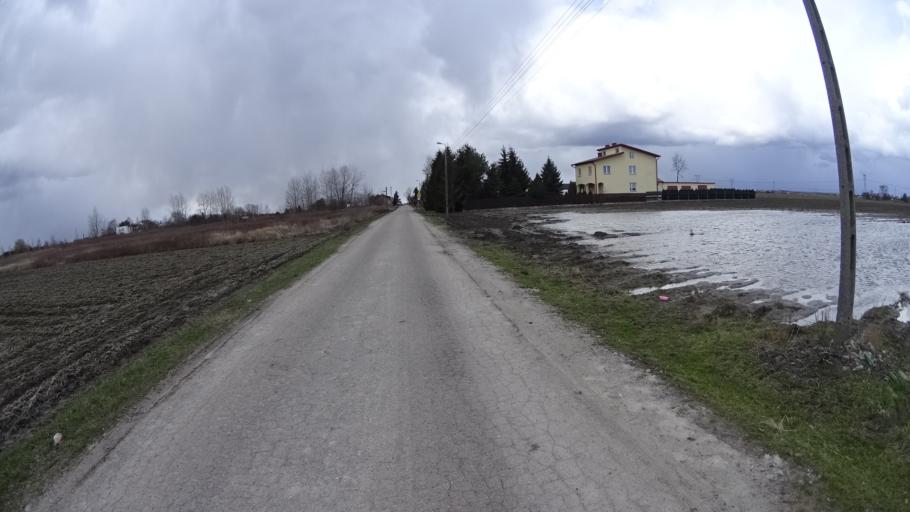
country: PL
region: Masovian Voivodeship
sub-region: Powiat warszawski zachodni
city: Jozefow
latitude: 52.2207
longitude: 20.6883
